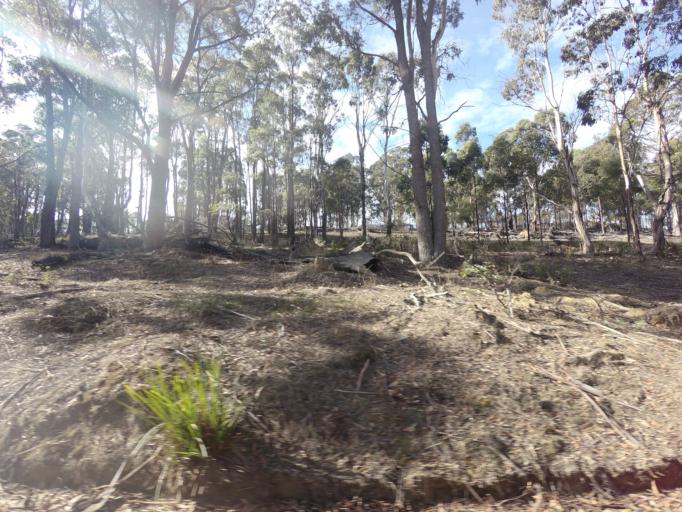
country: AU
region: Tasmania
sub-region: Sorell
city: Sorell
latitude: -42.5181
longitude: 147.4711
